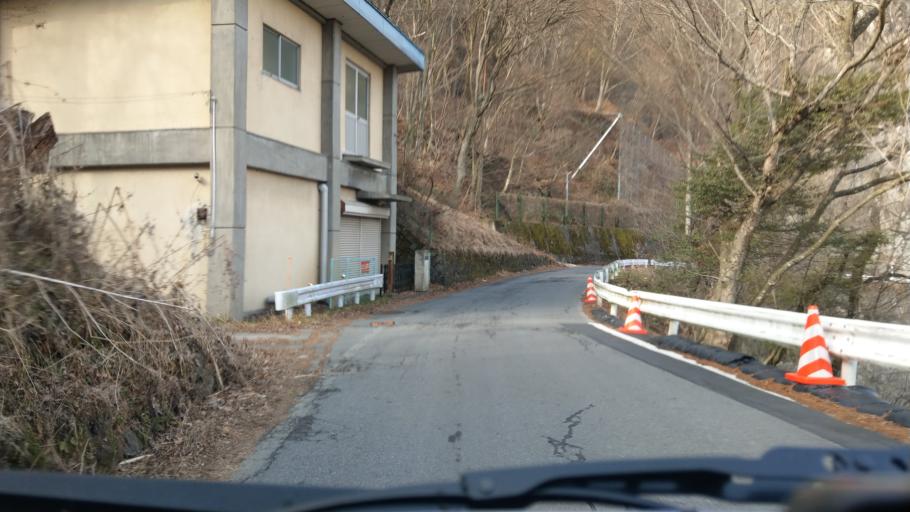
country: JP
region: Nagano
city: Komoro
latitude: 36.3295
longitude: 138.3916
